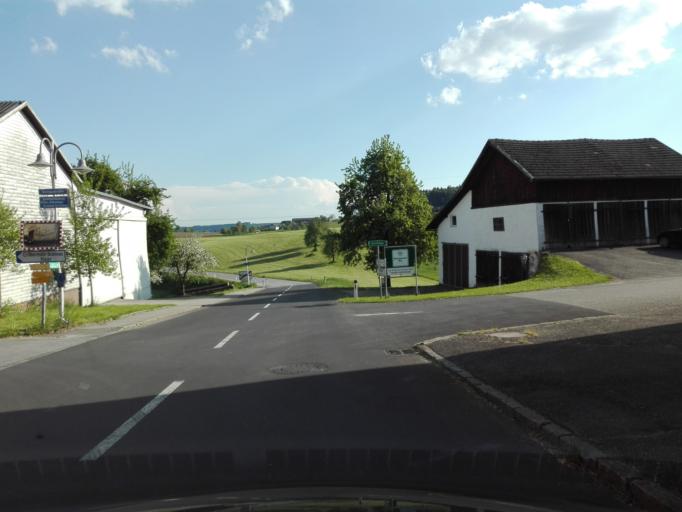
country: AT
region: Upper Austria
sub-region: Politischer Bezirk Rohrbach
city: Atzesberg
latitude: 48.4641
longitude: 13.8826
